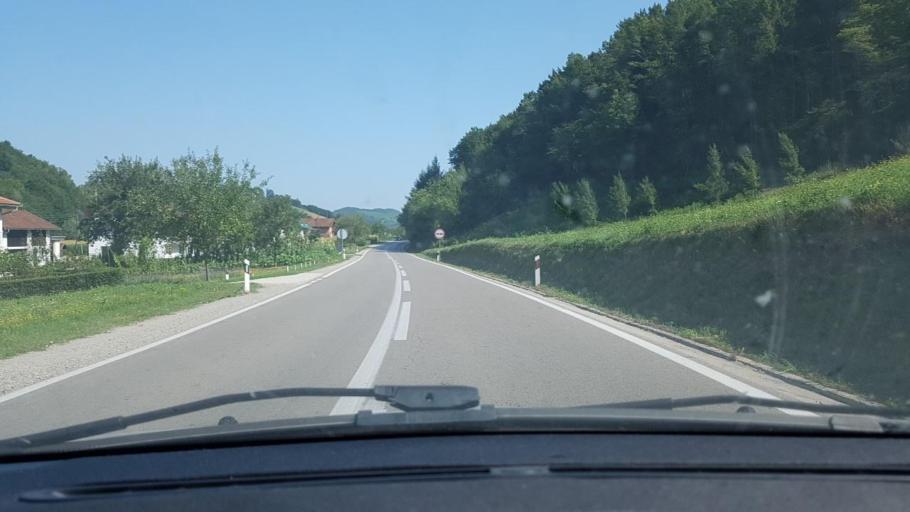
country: BA
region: Federation of Bosnia and Herzegovina
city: Pecigrad
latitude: 45.0770
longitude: 15.8897
